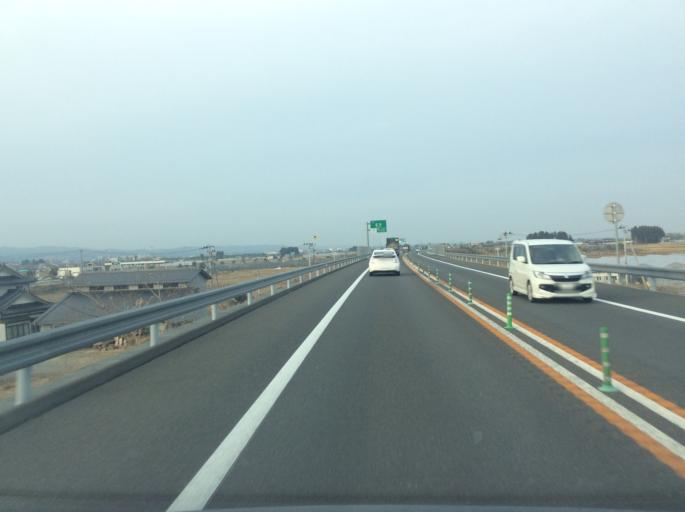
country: JP
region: Miyagi
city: Iwanuma
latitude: 38.0821
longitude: 140.8872
